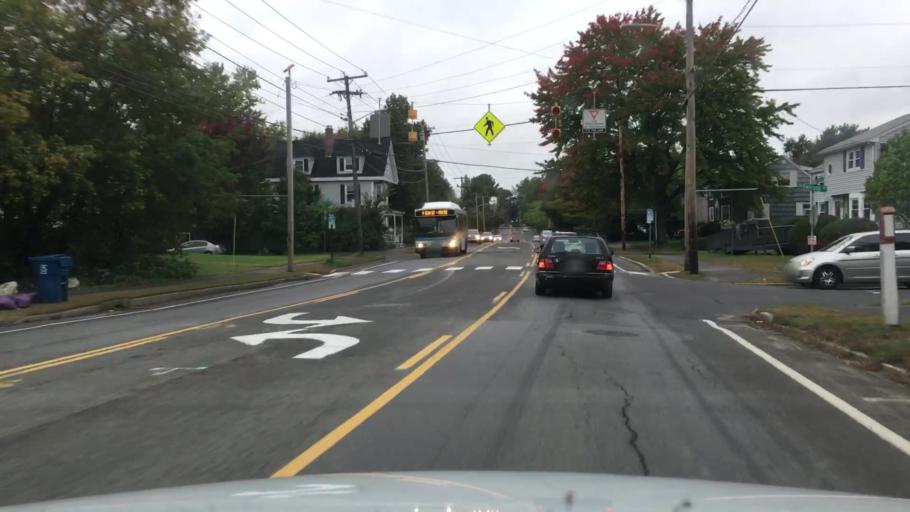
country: US
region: Maine
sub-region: Cumberland County
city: South Portland Gardens
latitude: 43.6711
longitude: -70.3080
